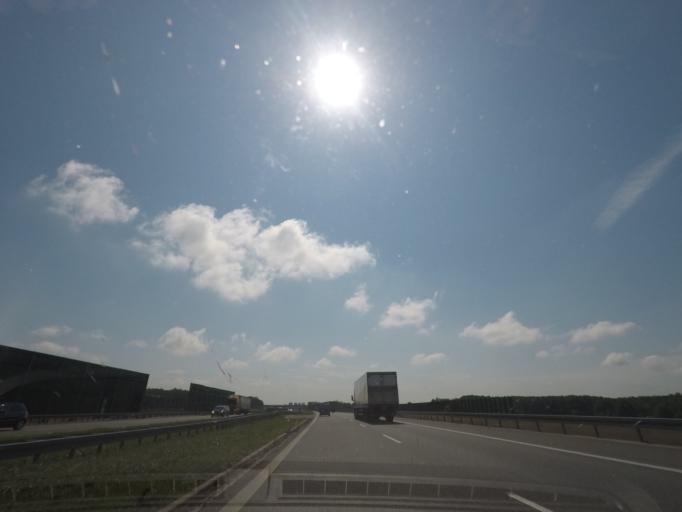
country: PL
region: Kujawsko-Pomorskie
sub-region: Powiat wloclawski
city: Baruchowo
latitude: 52.4453
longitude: 19.2286
